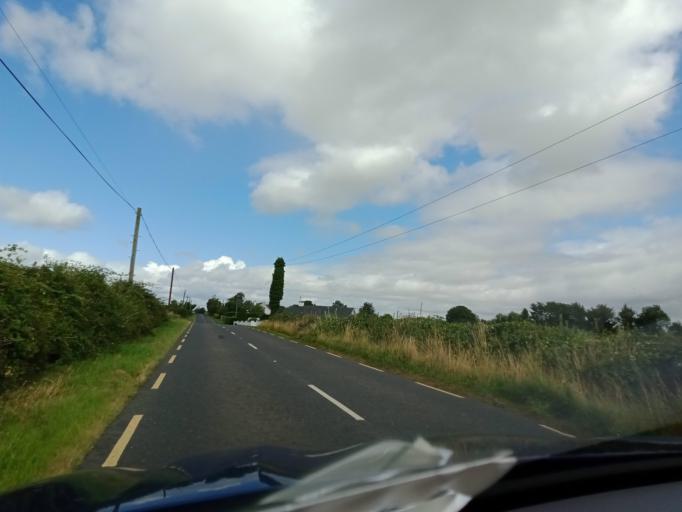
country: IE
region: Leinster
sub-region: Laois
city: Portlaoise
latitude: 52.9750
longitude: -7.2918
